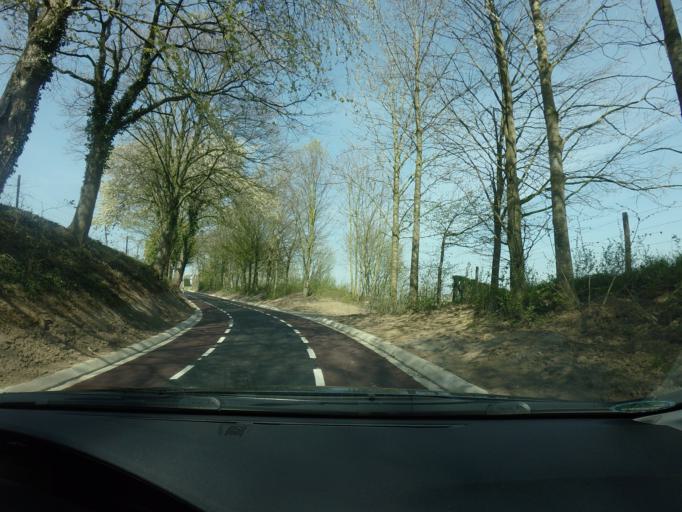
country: NL
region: Limburg
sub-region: Eijsden-Margraten
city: Margraten
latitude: 50.8307
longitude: 5.8005
